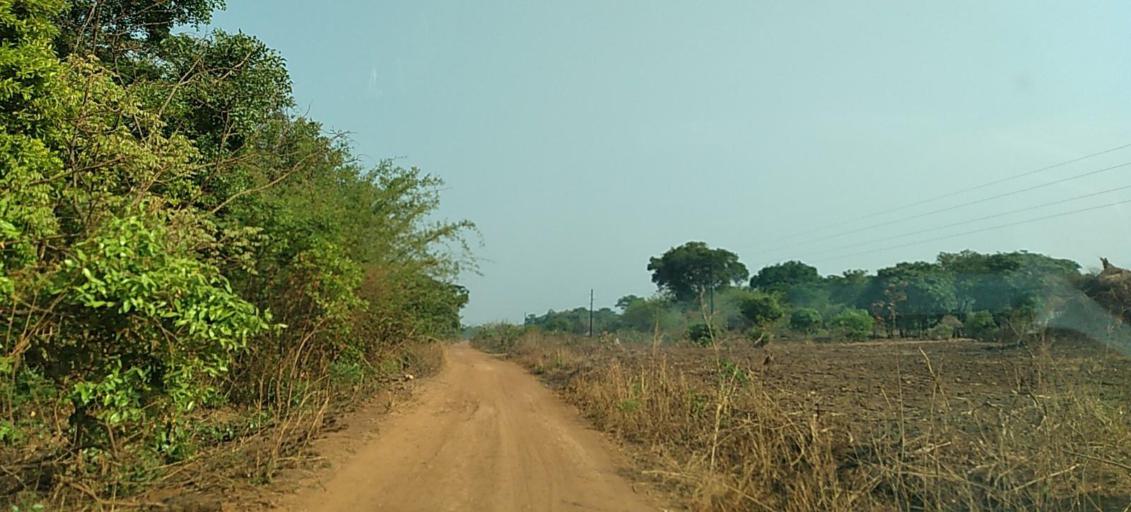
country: ZM
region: Copperbelt
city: Chingola
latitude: -12.8488
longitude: 27.5503
